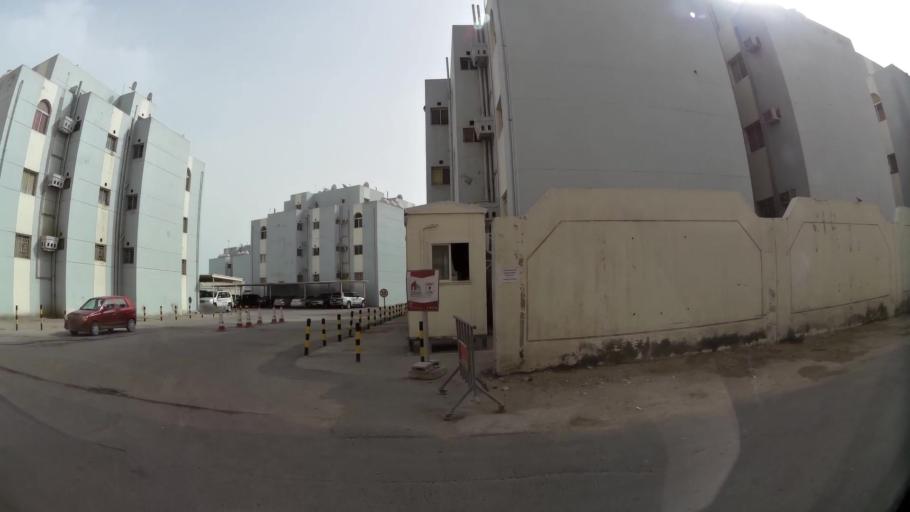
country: QA
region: Baladiyat ad Dawhah
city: Doha
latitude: 25.2754
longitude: 51.5507
